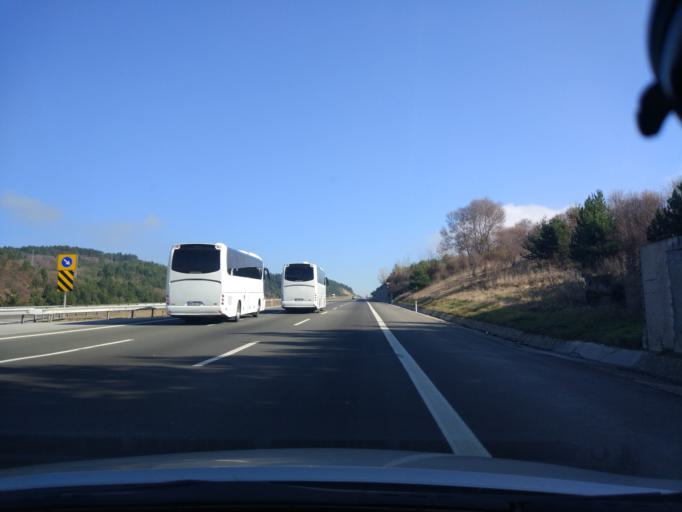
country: TR
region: Bolu
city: Yenicaga
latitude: 40.7460
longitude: 31.8791
